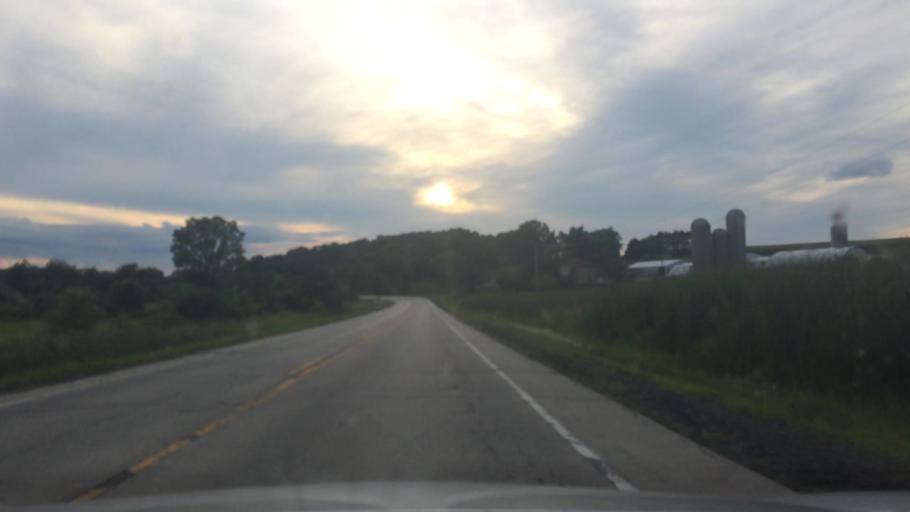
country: US
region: Wisconsin
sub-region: Columbia County
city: Lodi
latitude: 43.3193
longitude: -89.5118
